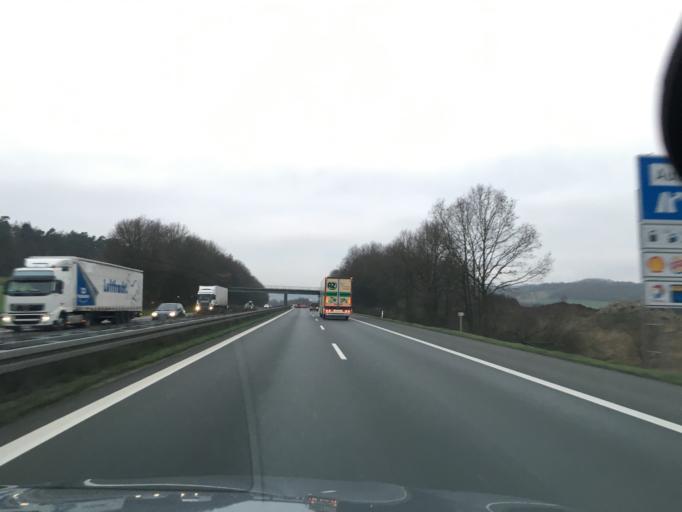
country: DE
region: Bavaria
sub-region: Regierungsbezirk Unterfranken
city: Geiselwind
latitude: 49.7669
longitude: 10.5035
